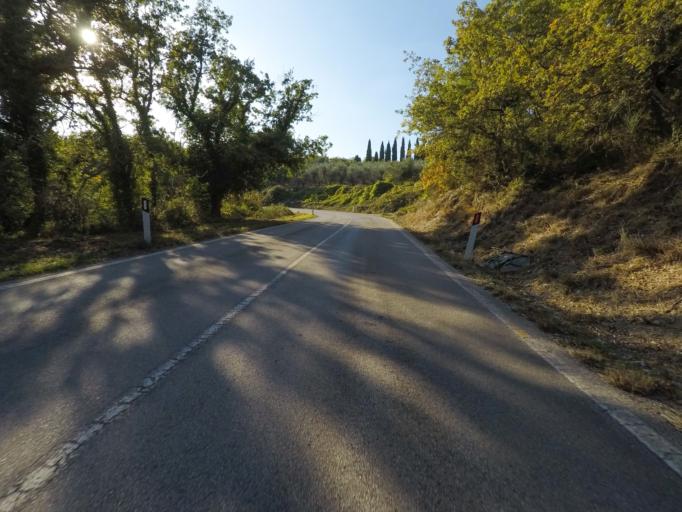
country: IT
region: Tuscany
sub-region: Provincia di Siena
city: Radda in Chianti
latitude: 43.4573
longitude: 11.3854
